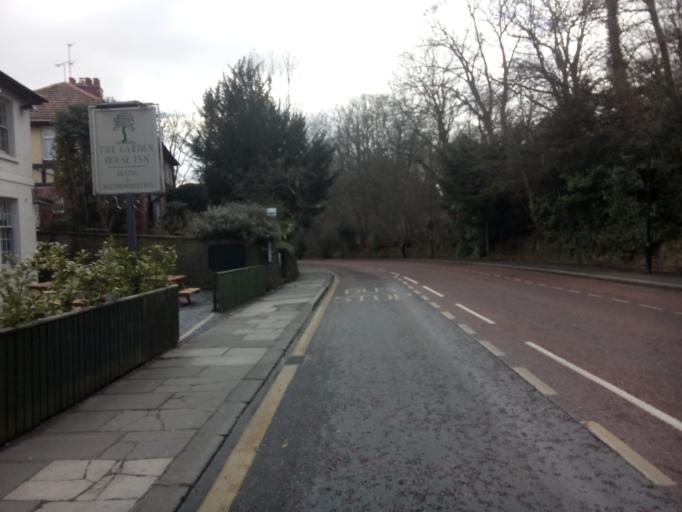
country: GB
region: England
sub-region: County Durham
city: Durham
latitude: 54.7831
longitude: -1.5860
